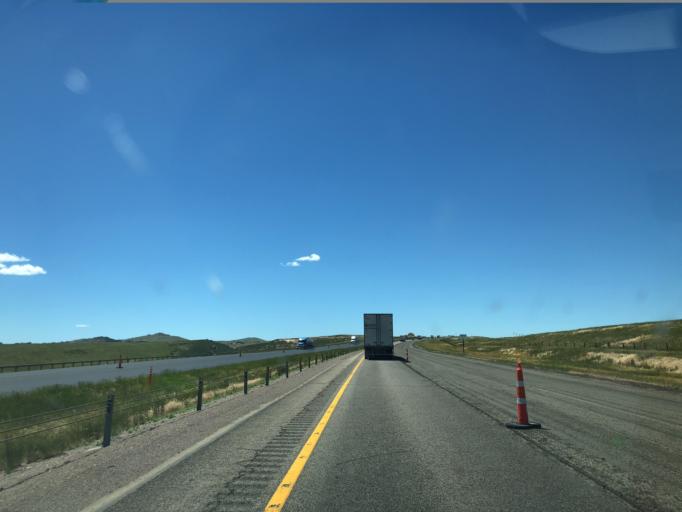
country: US
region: Wyoming
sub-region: Laramie County
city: Cheyenne
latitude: 41.0988
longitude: -105.1328
